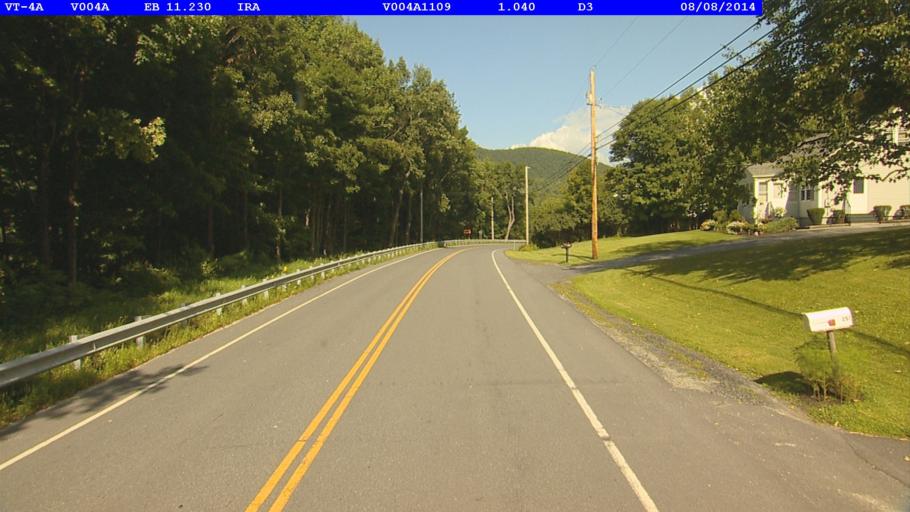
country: US
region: Vermont
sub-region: Rutland County
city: West Rutland
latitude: 43.6072
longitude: -73.0933
